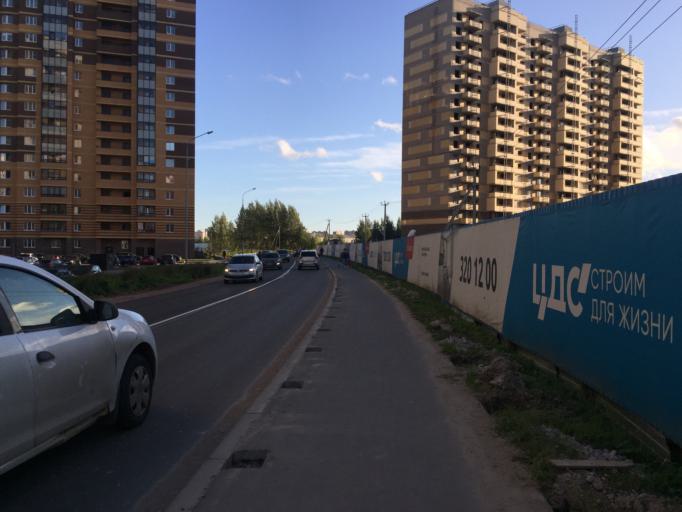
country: RU
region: Leningrad
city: Murino
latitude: 60.0606
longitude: 30.4575
